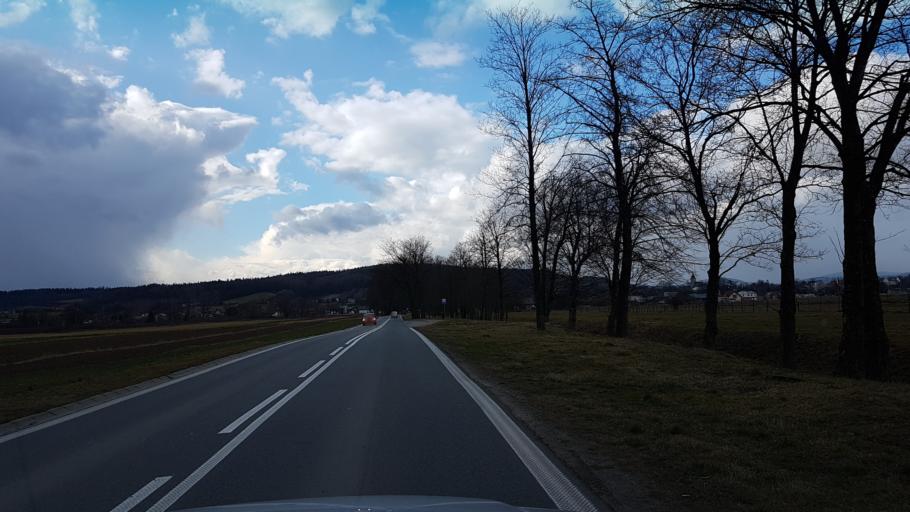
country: PL
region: Lesser Poland Voivodeship
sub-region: Powiat nowosadecki
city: Stary Sacz
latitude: 49.5525
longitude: 20.6515
